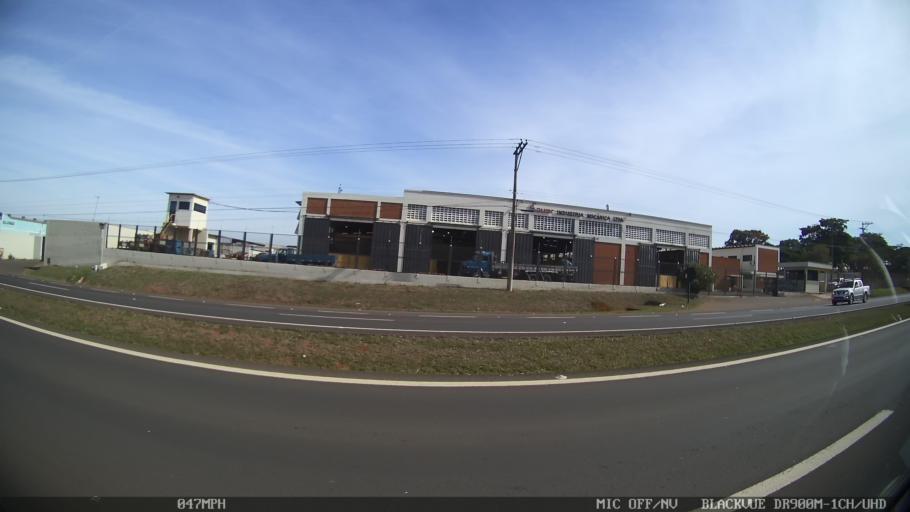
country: BR
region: Sao Paulo
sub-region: Piracicaba
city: Piracicaba
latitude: -22.7663
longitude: -47.6458
